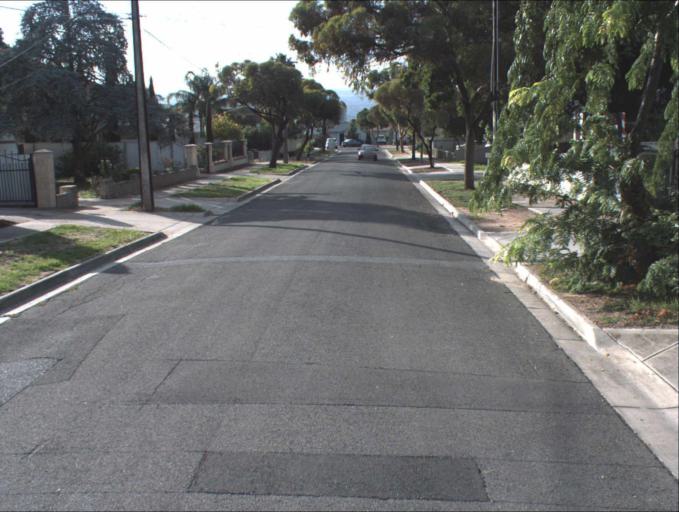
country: AU
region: South Australia
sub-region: Port Adelaide Enfield
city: Klemzig
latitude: -34.8735
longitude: 138.6303
